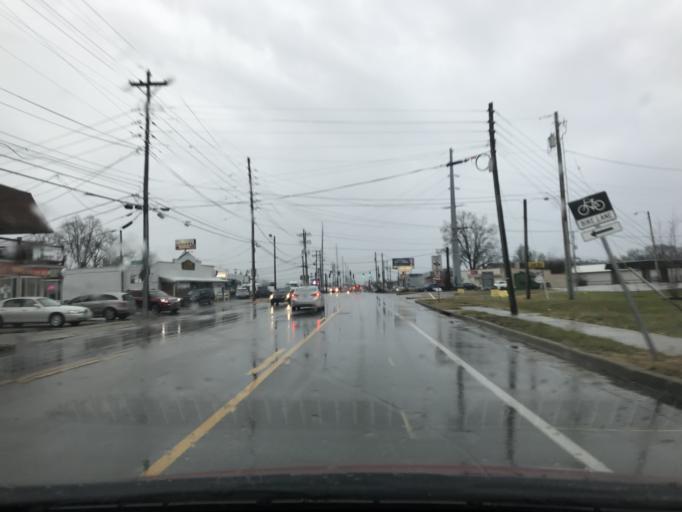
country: US
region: Kentucky
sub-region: Jefferson County
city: Buechel
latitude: 38.1959
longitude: -85.6544
